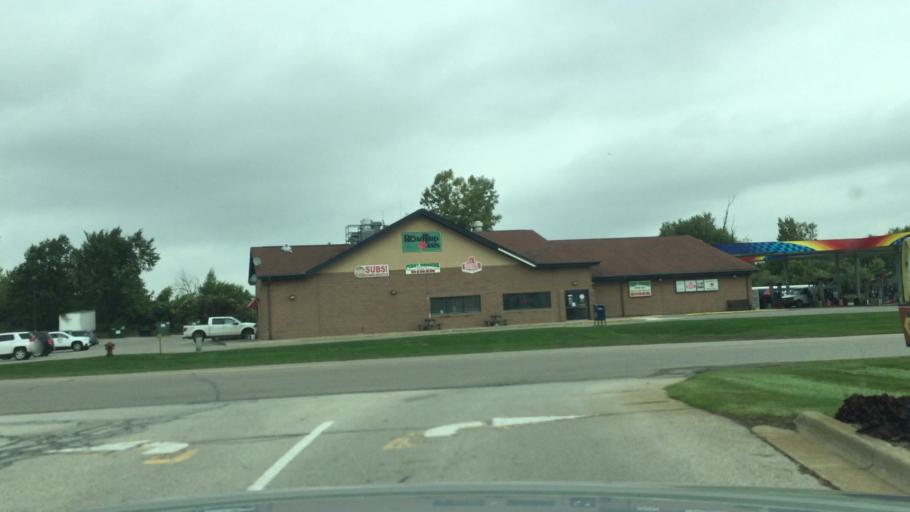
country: US
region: Michigan
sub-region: Shiawassee County
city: Perry
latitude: 42.8353
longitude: -84.2211
